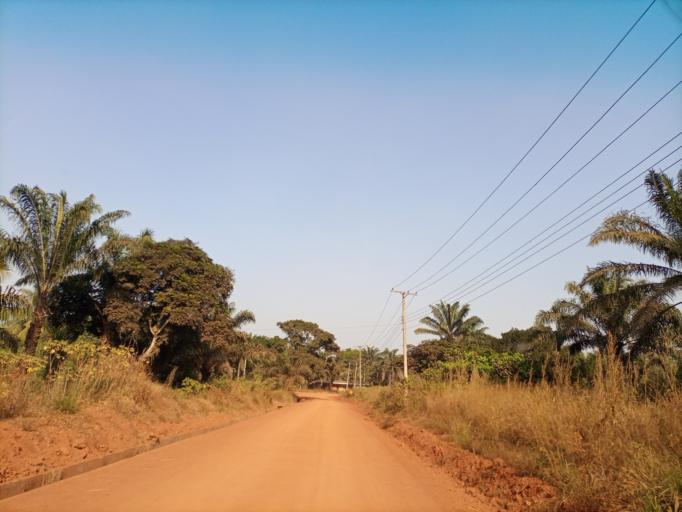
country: NG
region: Enugu
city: Opi
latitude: 6.7781
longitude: 7.3882
